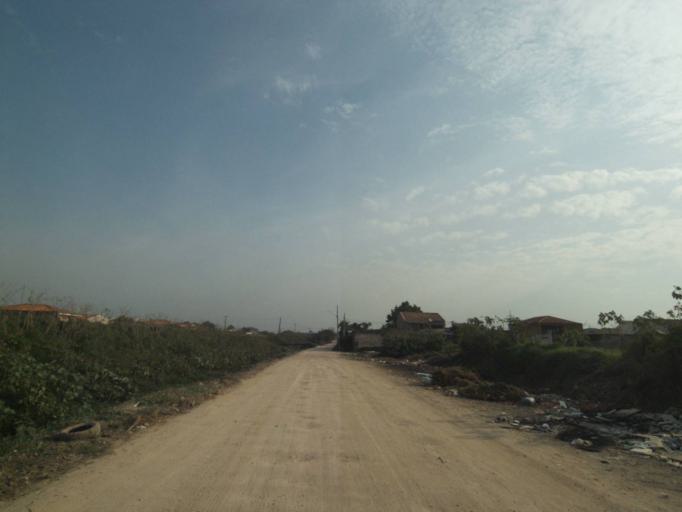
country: BR
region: Parana
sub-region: Sao Jose Dos Pinhais
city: Sao Jose dos Pinhais
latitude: -25.4950
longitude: -49.2046
